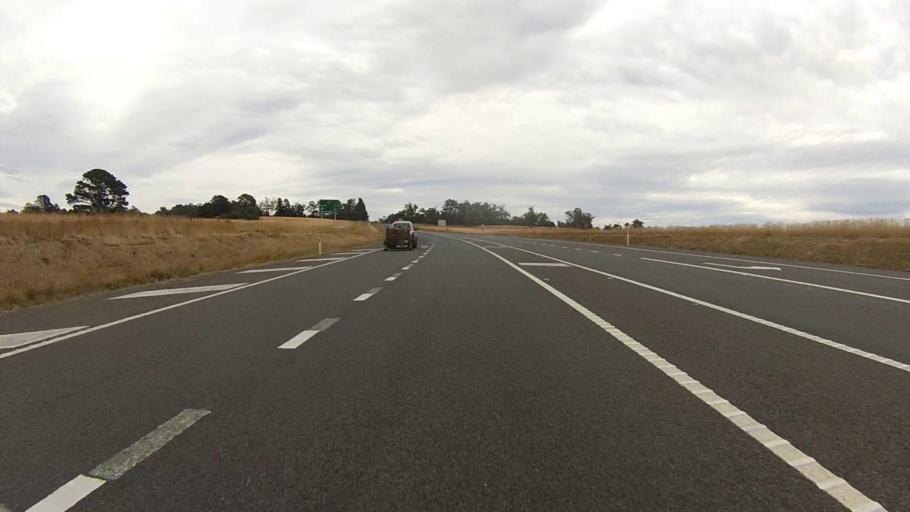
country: AU
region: Tasmania
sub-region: Northern Midlands
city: Evandale
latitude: -41.8354
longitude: 147.4471
